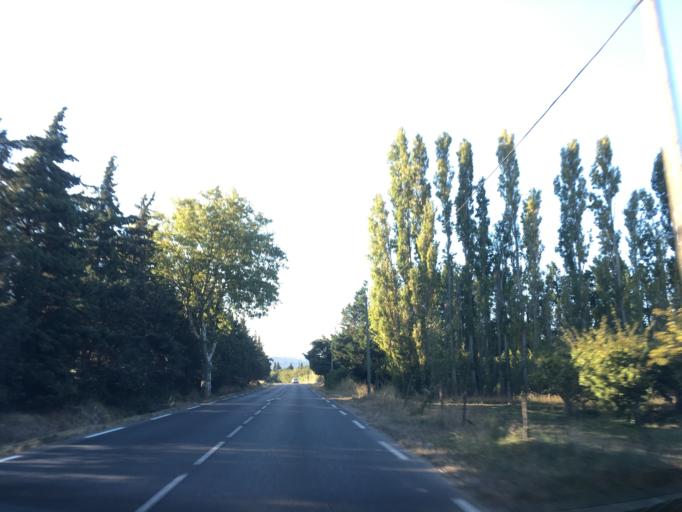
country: FR
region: Provence-Alpes-Cote d'Azur
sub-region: Departement des Bouches-du-Rhone
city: Senas
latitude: 43.7285
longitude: 5.0827
